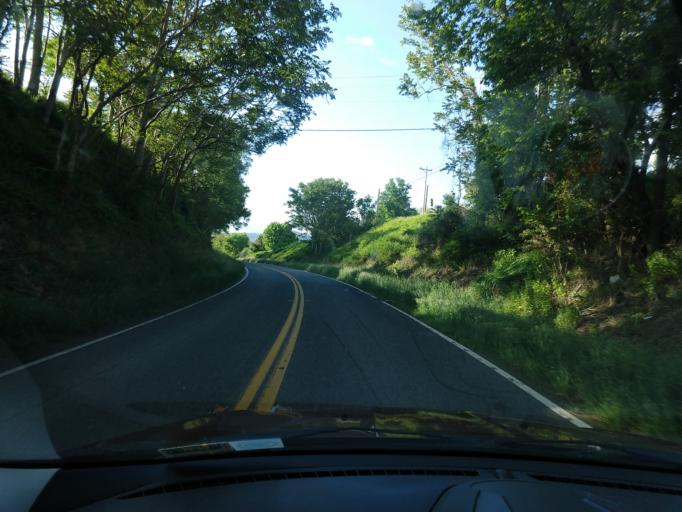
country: US
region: Virginia
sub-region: Wythe County
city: Wytheville
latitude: 36.8394
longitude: -80.9658
